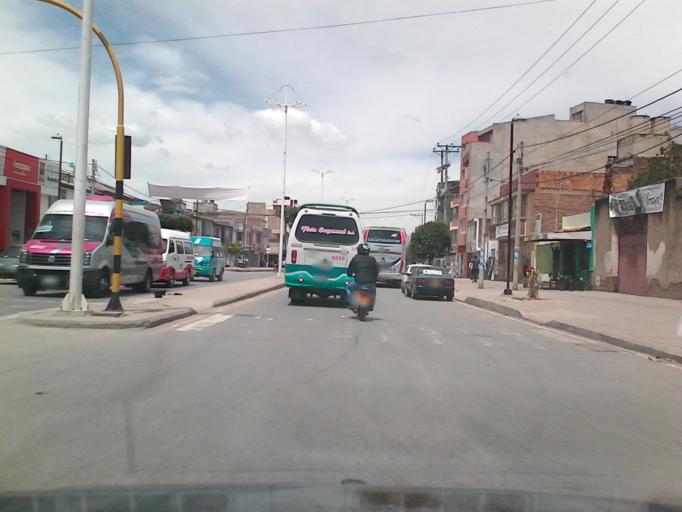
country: CO
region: Boyaca
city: Sogamoso
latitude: 5.7191
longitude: -72.9358
